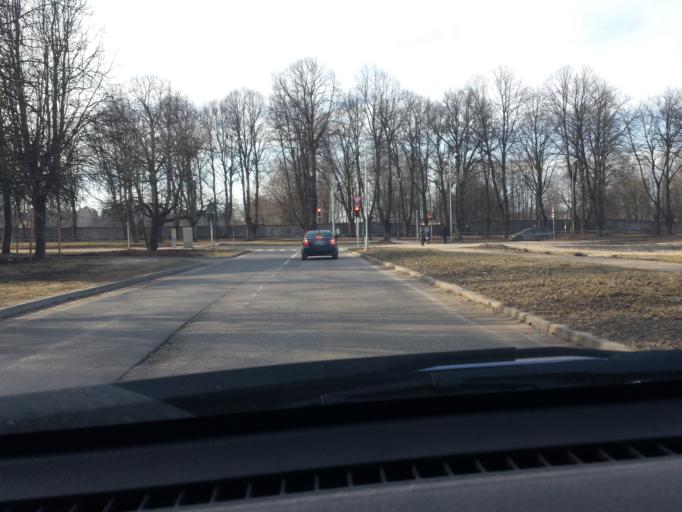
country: LV
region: Riga
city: Jaunciems
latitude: 56.9892
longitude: 24.1662
